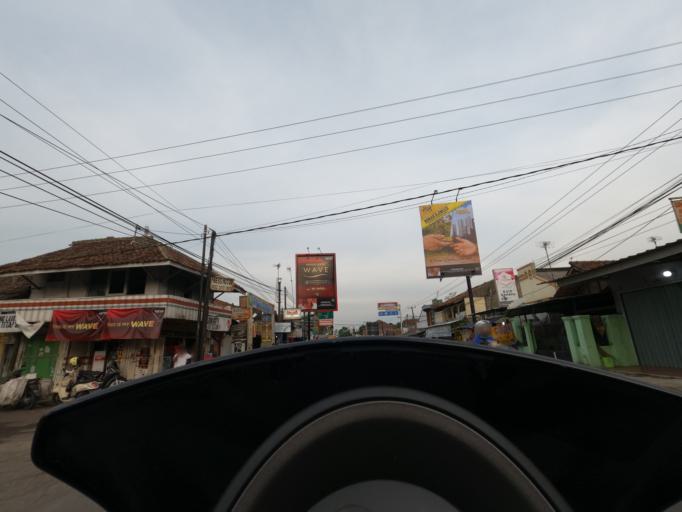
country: ID
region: West Java
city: Lembang
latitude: -6.6783
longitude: 107.6877
